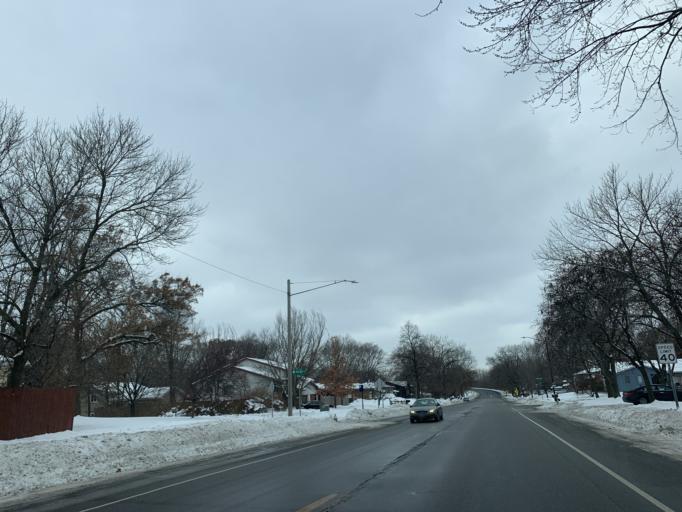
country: US
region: Minnesota
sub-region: Anoka County
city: Blaine
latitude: 45.1639
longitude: -93.2788
